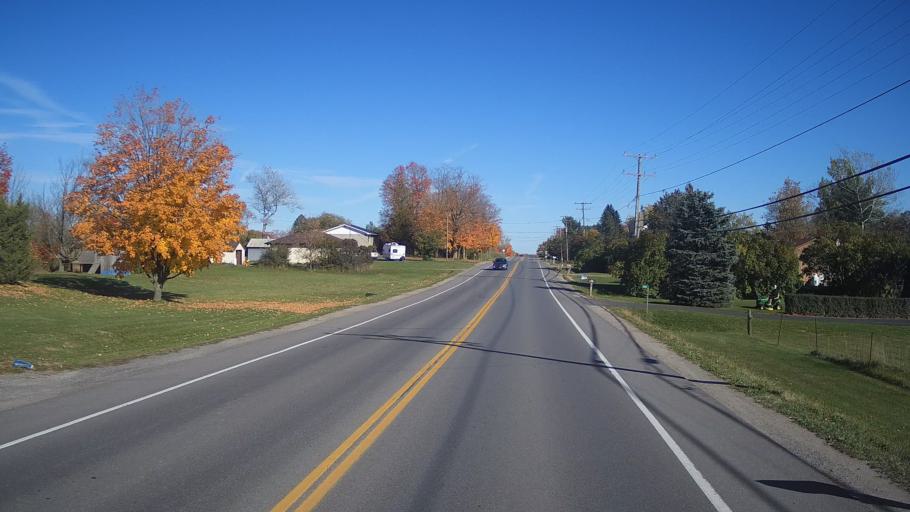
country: CA
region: Ontario
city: Kingston
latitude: 44.4072
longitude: -76.5823
